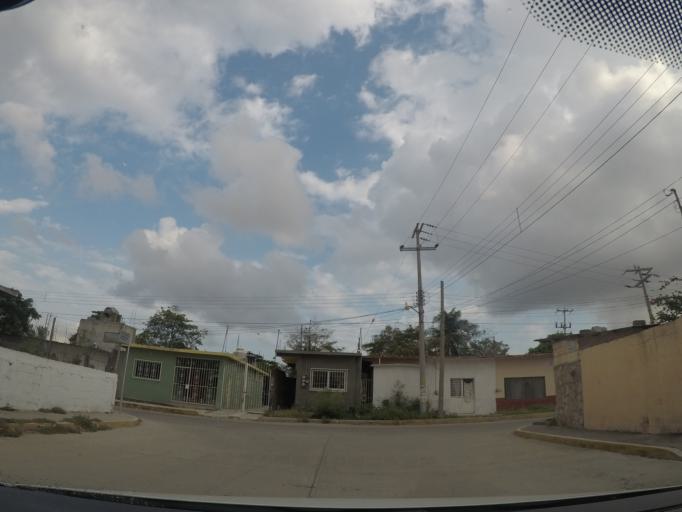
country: MX
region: Oaxaca
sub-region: Salina Cruz
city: Salina Cruz
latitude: 16.2110
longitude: -95.2073
